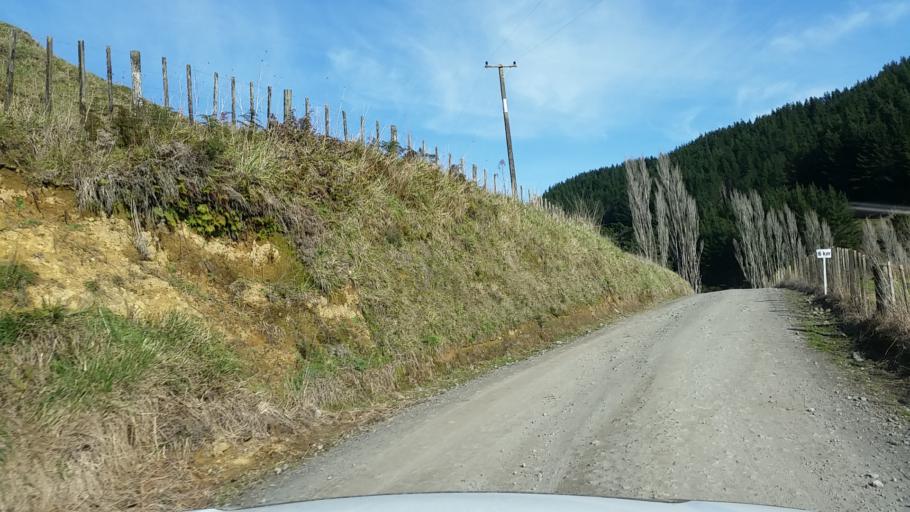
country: NZ
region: Taranaki
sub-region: South Taranaki District
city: Eltham
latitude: -39.3557
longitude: 174.5128
